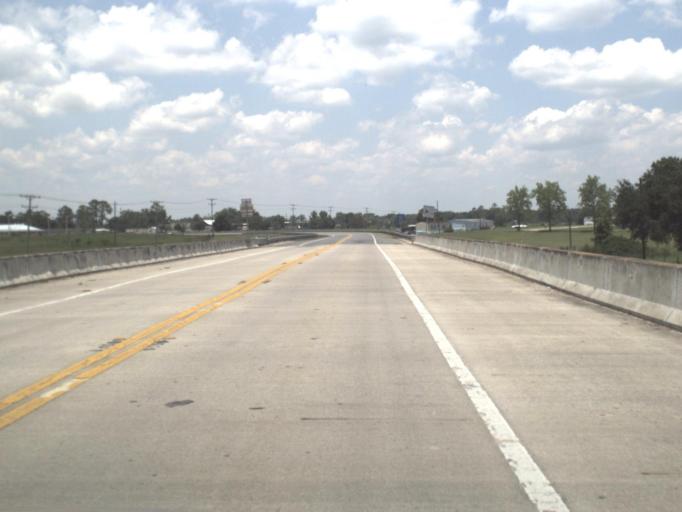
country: US
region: Florida
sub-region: Bradford County
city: Starke
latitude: 30.0666
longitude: -82.1838
